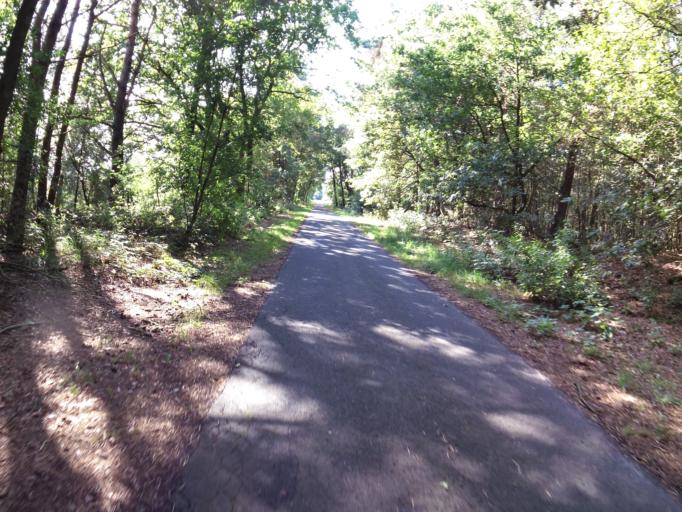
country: DE
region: Lower Saxony
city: Sandbostel
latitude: 53.3939
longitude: 9.1209
